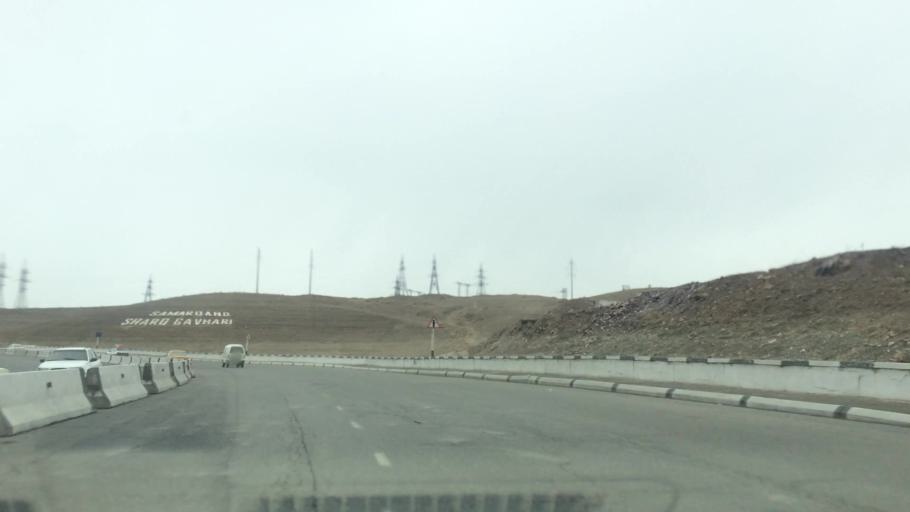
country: UZ
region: Samarqand
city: Jomboy
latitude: 39.6891
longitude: 67.0532
